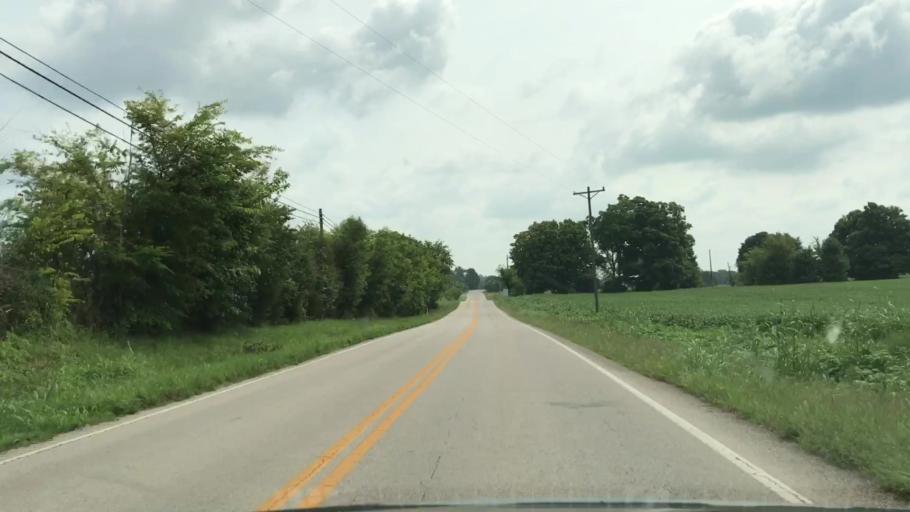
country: US
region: Kentucky
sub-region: Barren County
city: Cave City
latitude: 37.0921
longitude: -86.0952
